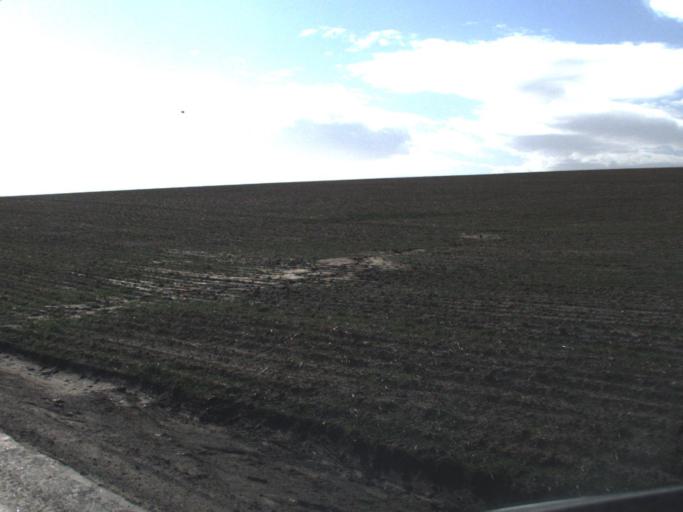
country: US
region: Washington
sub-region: Okanogan County
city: Coulee Dam
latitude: 47.5847
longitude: -118.7860
